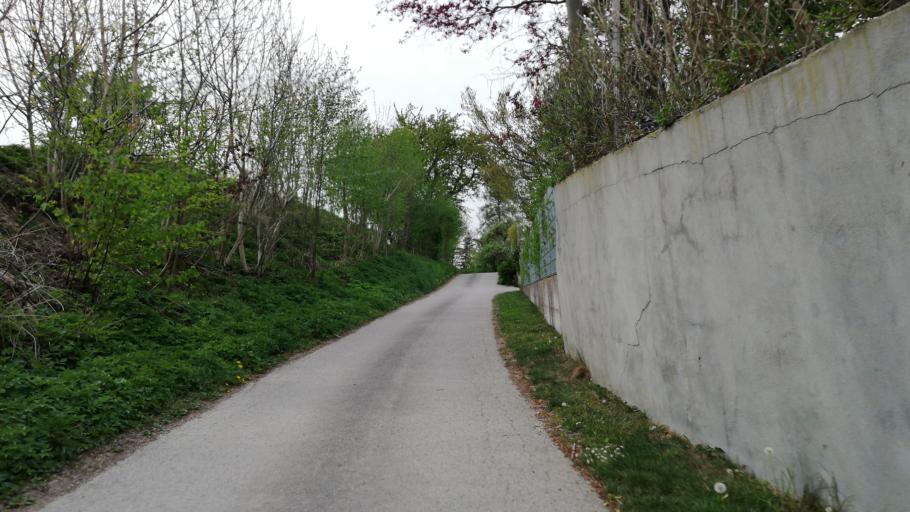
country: AT
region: Upper Austria
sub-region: Politischer Bezirk Grieskirchen
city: Bad Schallerbach
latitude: 48.1860
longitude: 13.9464
